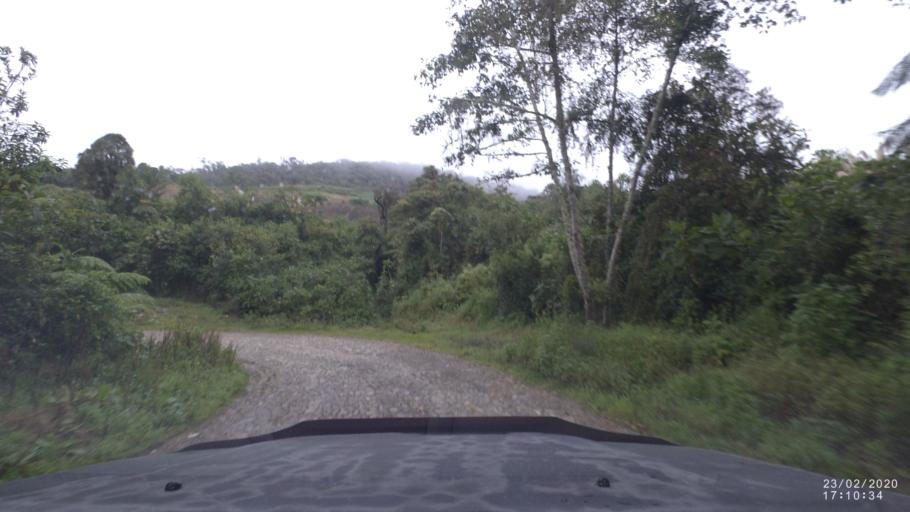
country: BO
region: Cochabamba
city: Colomi
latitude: -17.1309
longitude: -65.9481
